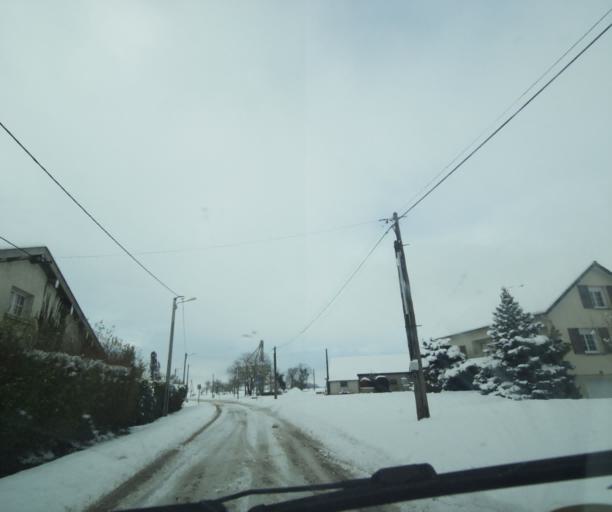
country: FR
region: Champagne-Ardenne
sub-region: Departement de la Haute-Marne
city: Montier-en-Der
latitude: 48.5251
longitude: 4.7117
